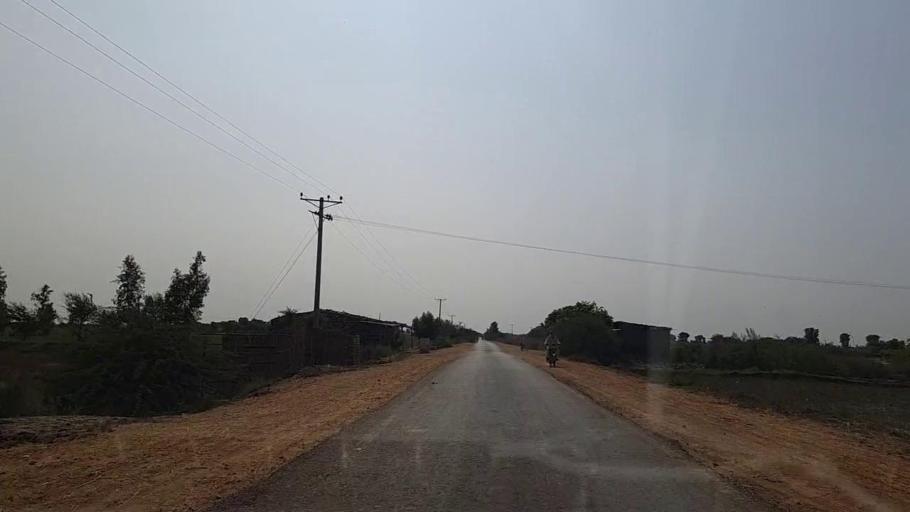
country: PK
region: Sindh
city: Chuhar Jamali
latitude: 24.3207
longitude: 67.9410
